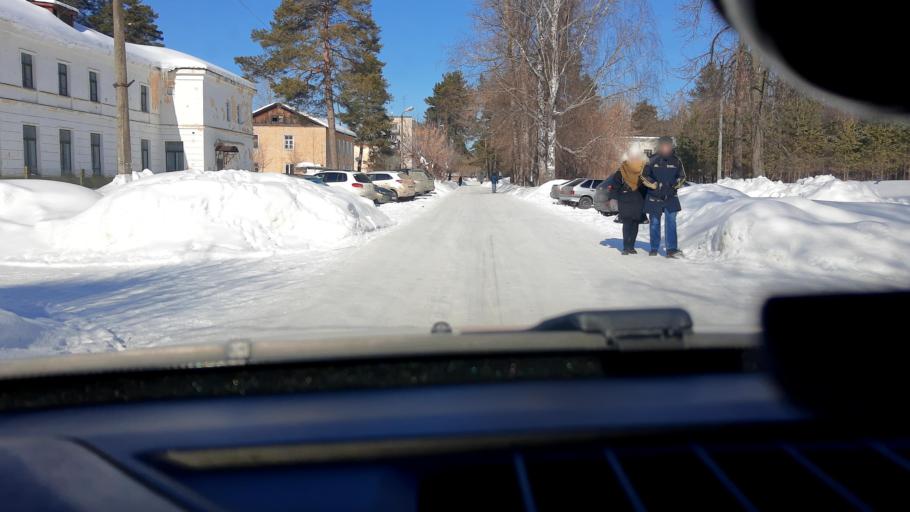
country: RU
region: Nizjnij Novgorod
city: Yuganets
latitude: 56.2516
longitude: 43.2327
